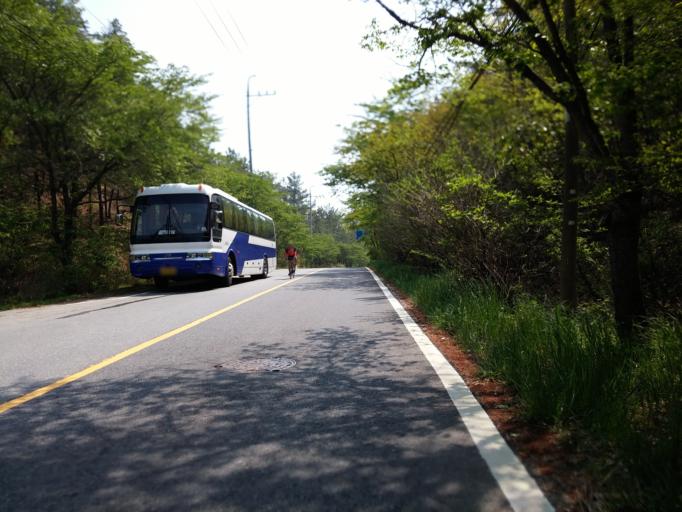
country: KR
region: Chungcheongbuk-do
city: Okcheon
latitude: 36.3910
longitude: 127.5293
